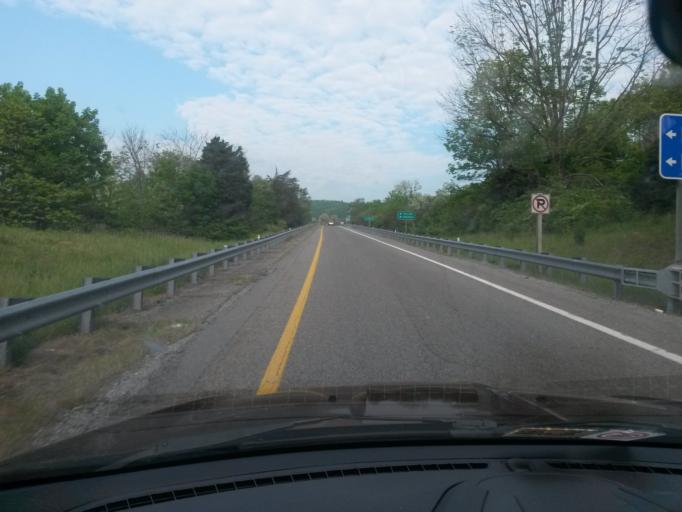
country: US
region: Virginia
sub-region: Roanoke County
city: Hollins
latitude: 37.3619
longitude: -79.9549
